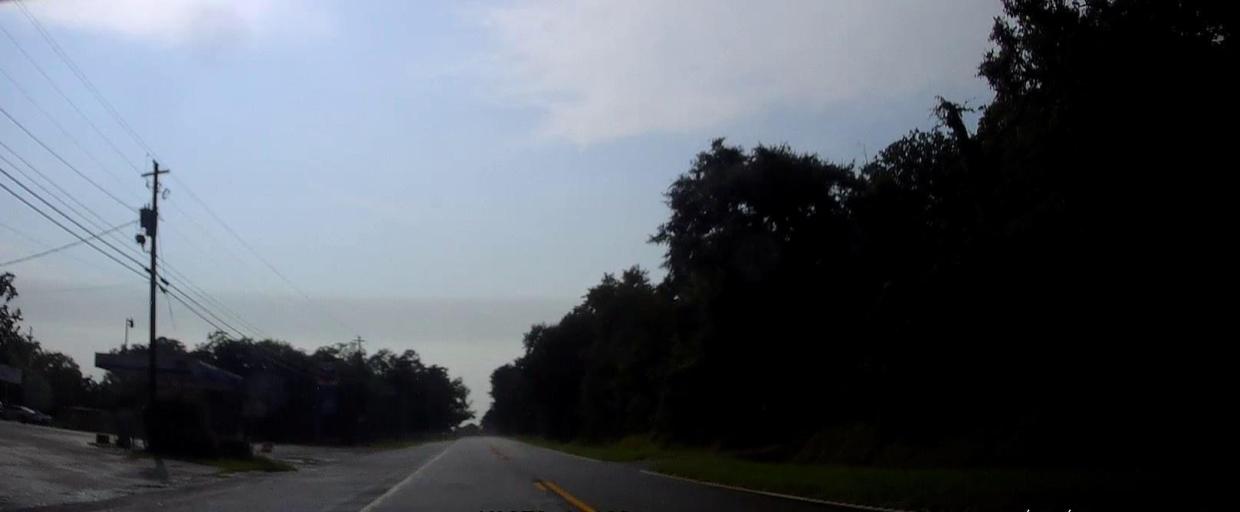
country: US
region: Georgia
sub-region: Twiggs County
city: Jeffersonville
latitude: 32.6033
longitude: -83.2483
